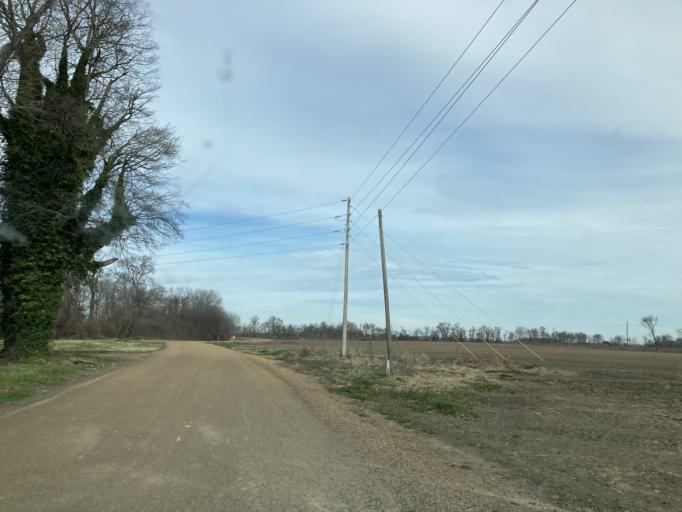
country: US
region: Mississippi
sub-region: Humphreys County
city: Belzoni
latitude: 33.1162
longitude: -90.6131
